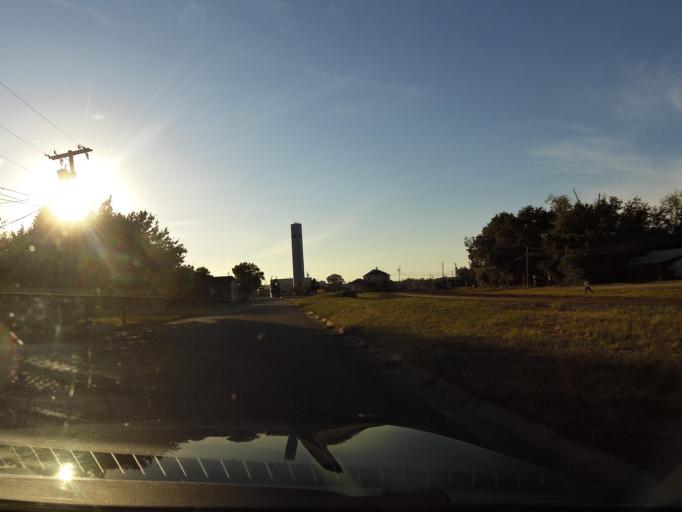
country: US
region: Alabama
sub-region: Houston County
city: Dothan
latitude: 31.2301
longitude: -85.3897
